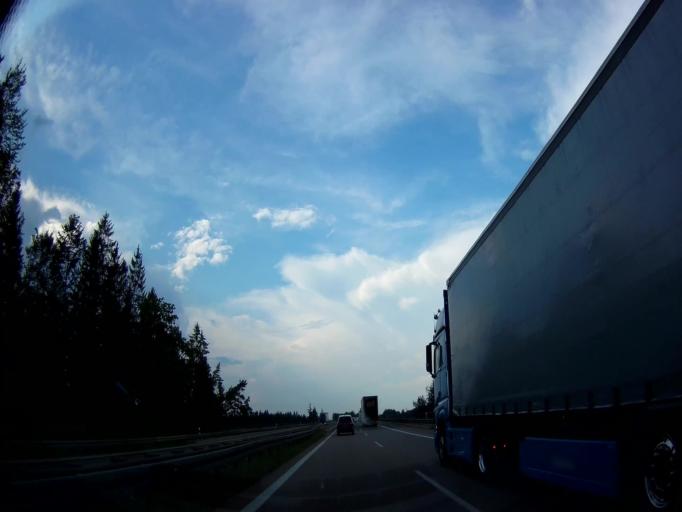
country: DE
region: Bavaria
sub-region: Upper Palatinate
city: Velburg
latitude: 49.2605
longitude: 11.6056
